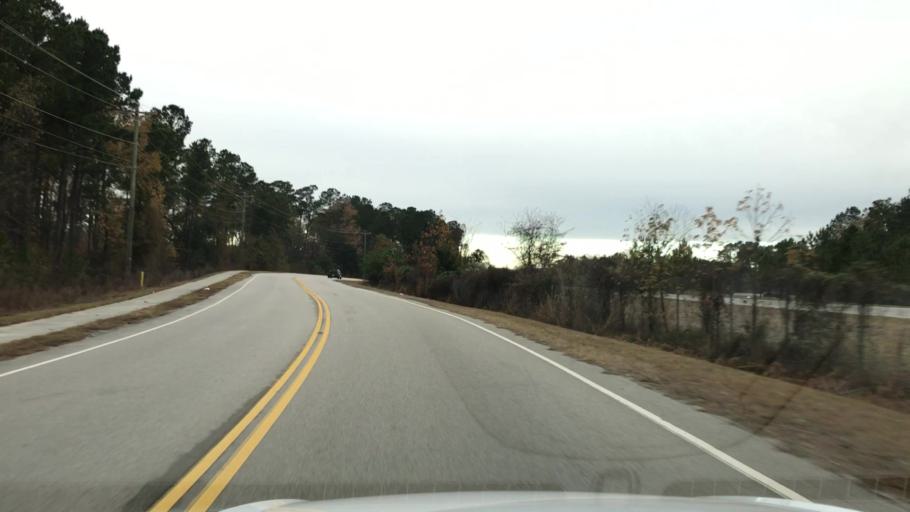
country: US
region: South Carolina
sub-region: Berkeley County
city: Ladson
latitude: 32.9768
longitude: -80.0779
